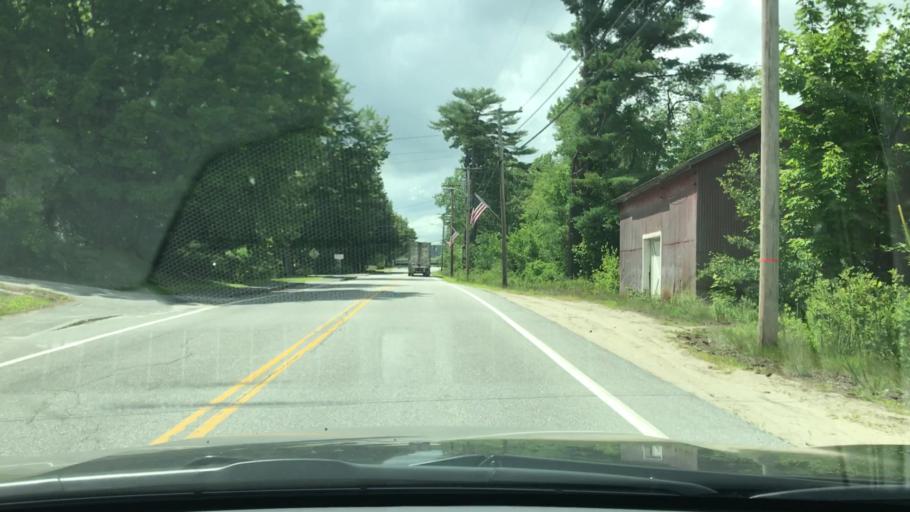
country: US
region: Maine
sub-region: Oxford County
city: Bethel
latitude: 44.4104
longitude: -70.7903
